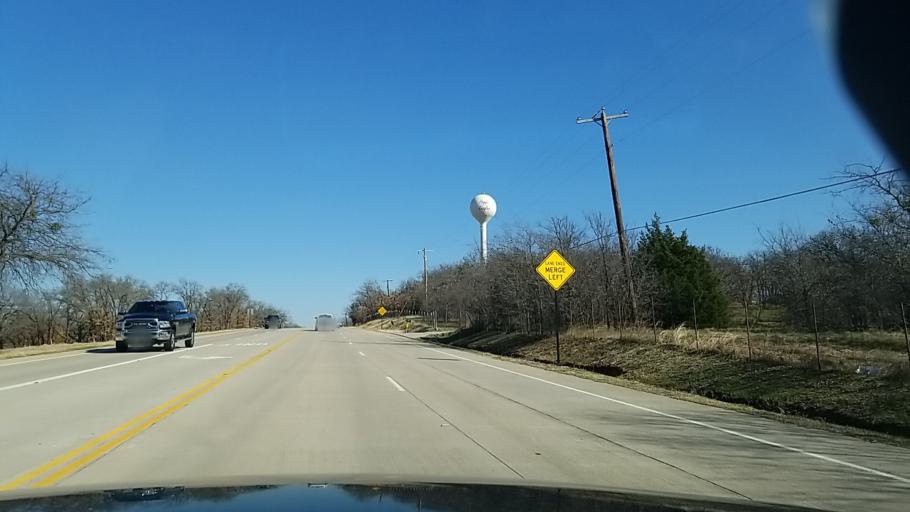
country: US
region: Texas
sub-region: Denton County
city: Argyle
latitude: 33.1282
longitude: -97.1796
